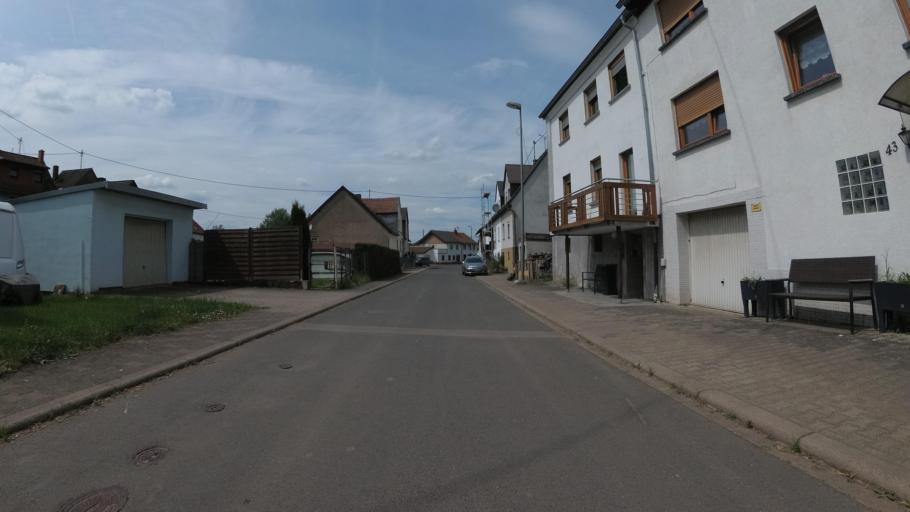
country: DE
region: Rheinland-Pfalz
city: Eckersweiler
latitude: 49.5749
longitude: 7.2969
